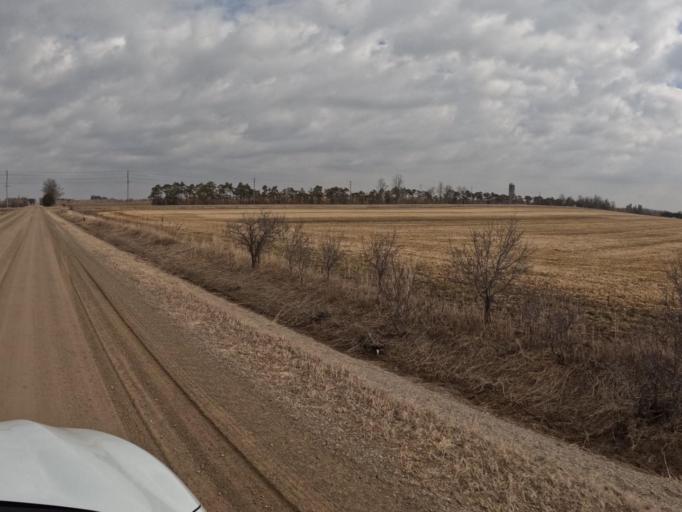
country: CA
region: Ontario
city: Orangeville
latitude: 43.9273
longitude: -80.1871
